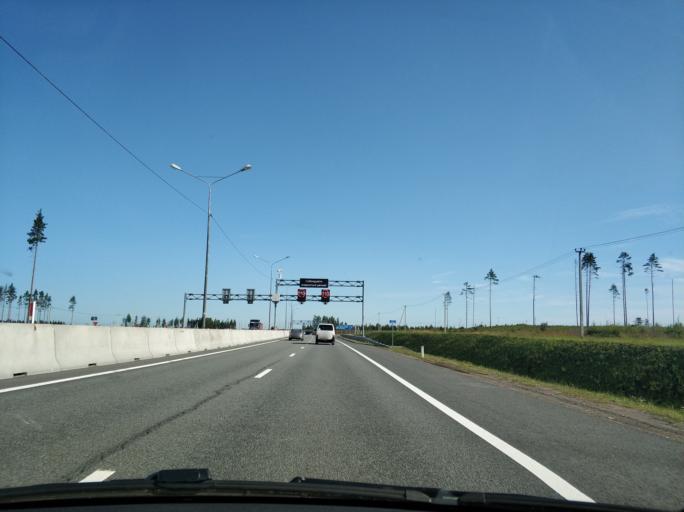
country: RU
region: Leningrad
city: Sosnovo
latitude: 60.4972
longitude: 30.1958
